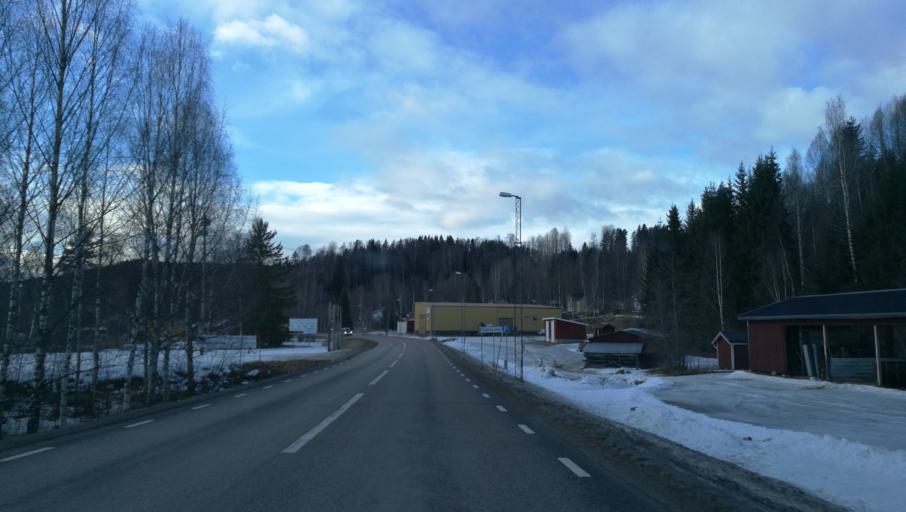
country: SE
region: Vaermland
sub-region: Torsby Kommun
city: Torsby
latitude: 60.7358
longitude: 12.8646
